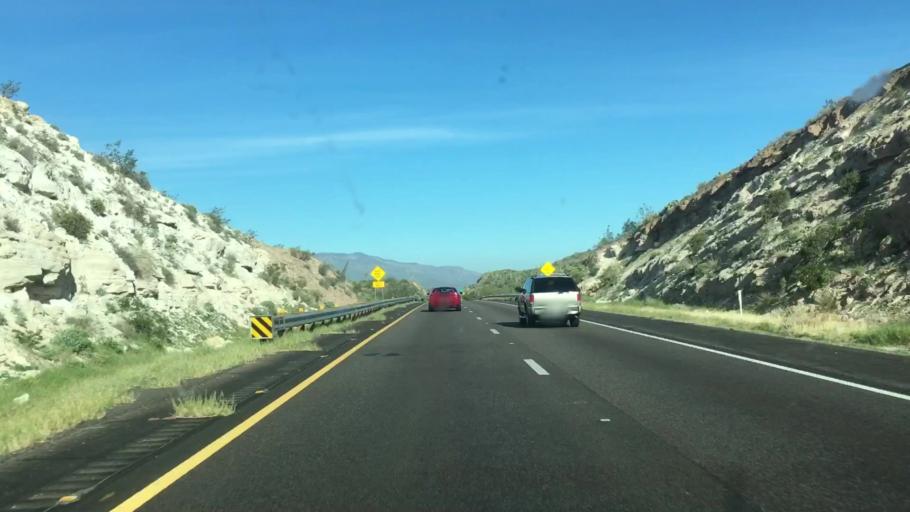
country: US
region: Arizona
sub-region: Maricopa County
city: New River
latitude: 33.9768
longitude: -112.1287
